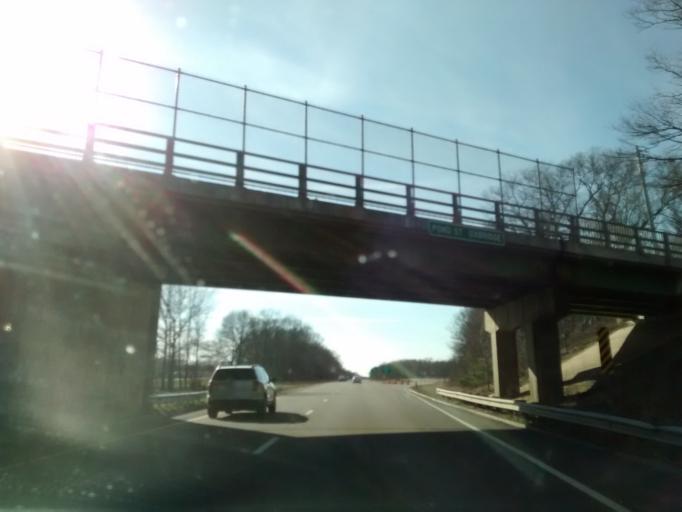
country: US
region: Massachusetts
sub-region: Worcester County
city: Uxbridge
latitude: 42.0608
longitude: -71.6506
